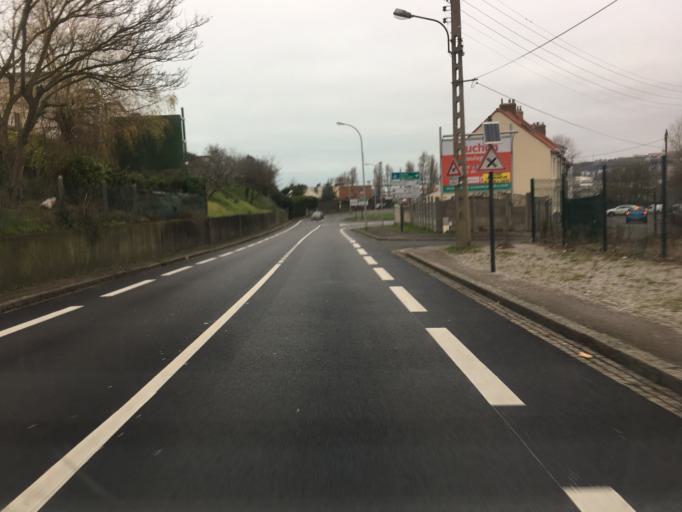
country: FR
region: Nord-Pas-de-Calais
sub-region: Departement du Pas-de-Calais
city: Outreau
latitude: 50.7172
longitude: 1.5908
